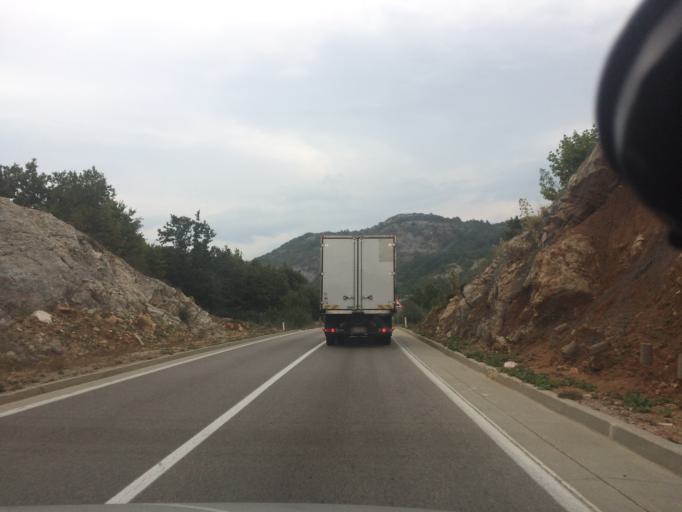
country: ME
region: Kotor
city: Risan
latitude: 42.6853
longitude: 18.6343
